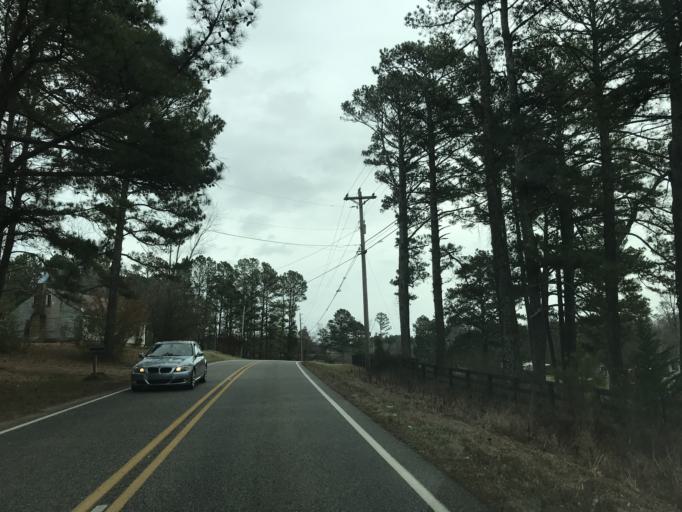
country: US
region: Georgia
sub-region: Fulton County
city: Milton
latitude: 34.2002
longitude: -84.3837
